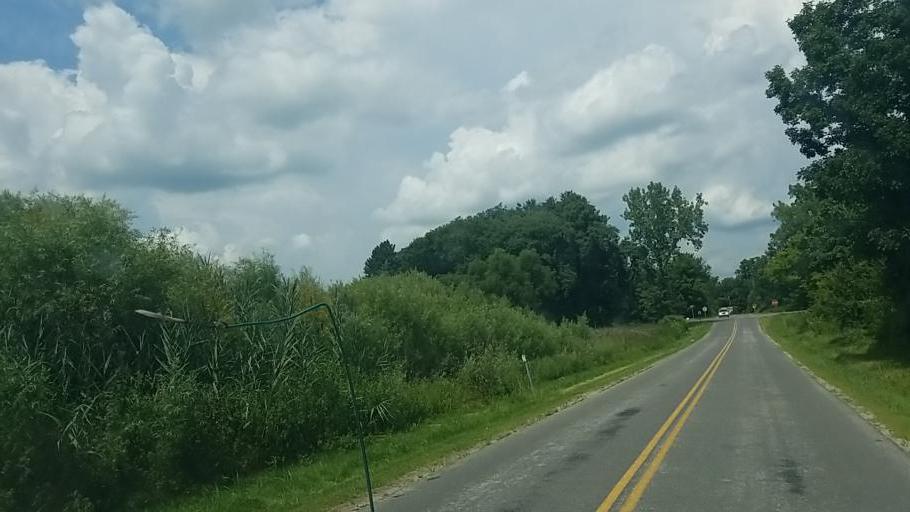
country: US
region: Ohio
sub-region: Medina County
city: Lodi
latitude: 41.0987
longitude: -82.0841
